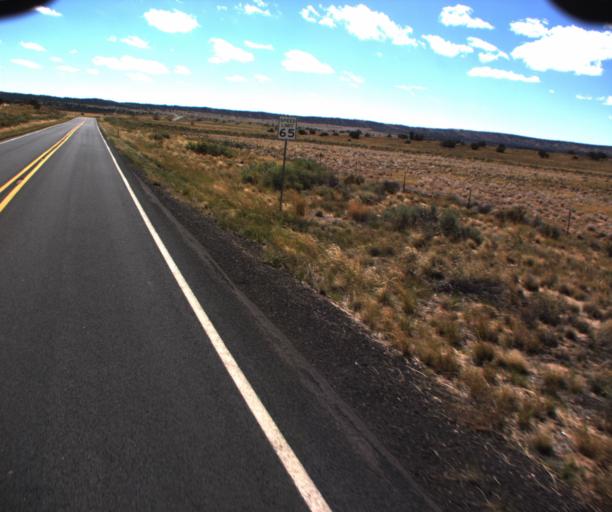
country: US
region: Arizona
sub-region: Apache County
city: Houck
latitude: 35.0624
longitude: -109.2811
